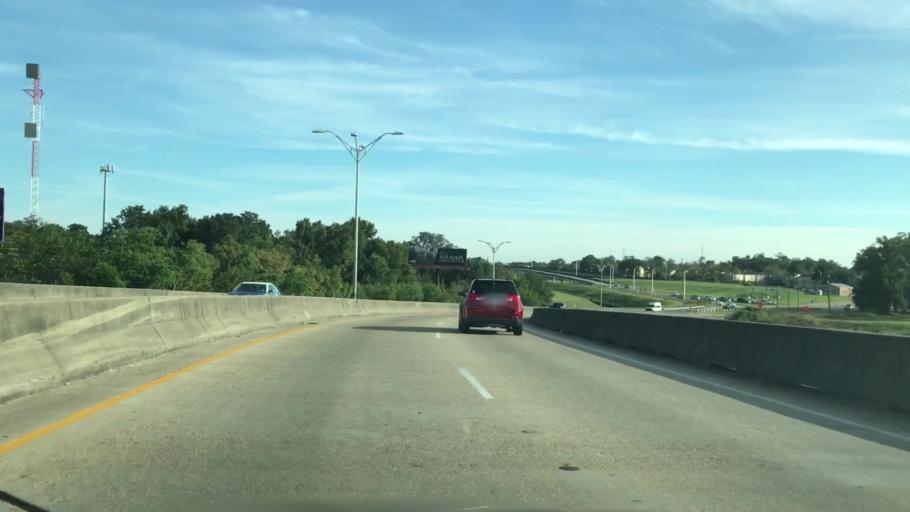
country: US
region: Louisiana
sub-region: Jefferson Parish
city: River Ridge
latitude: 29.9731
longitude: -90.2054
